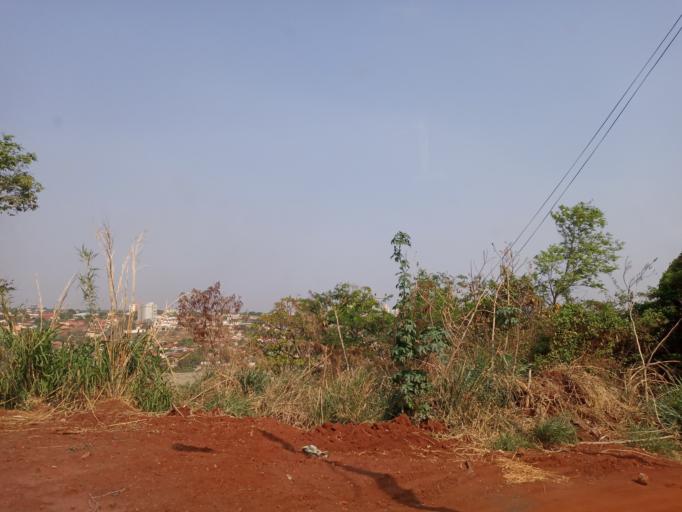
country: BR
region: Minas Gerais
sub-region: Ituiutaba
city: Ituiutaba
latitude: -18.9605
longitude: -49.4750
